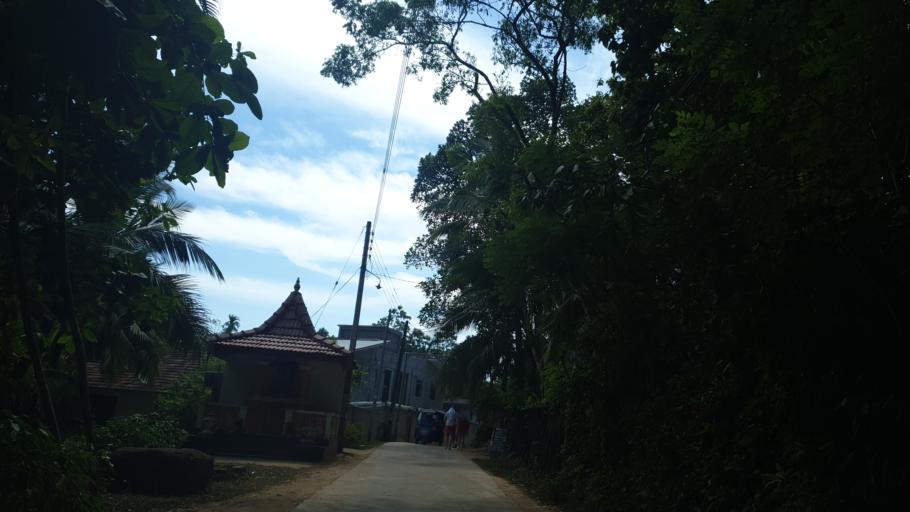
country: LK
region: Southern
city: Tangalla
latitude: 5.9660
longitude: 80.7073
